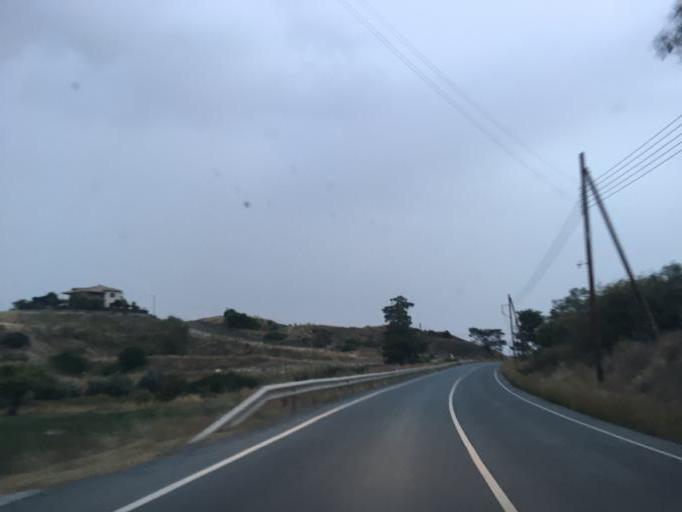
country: CY
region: Limassol
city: Parekklisha
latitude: 34.7648
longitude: 33.1629
